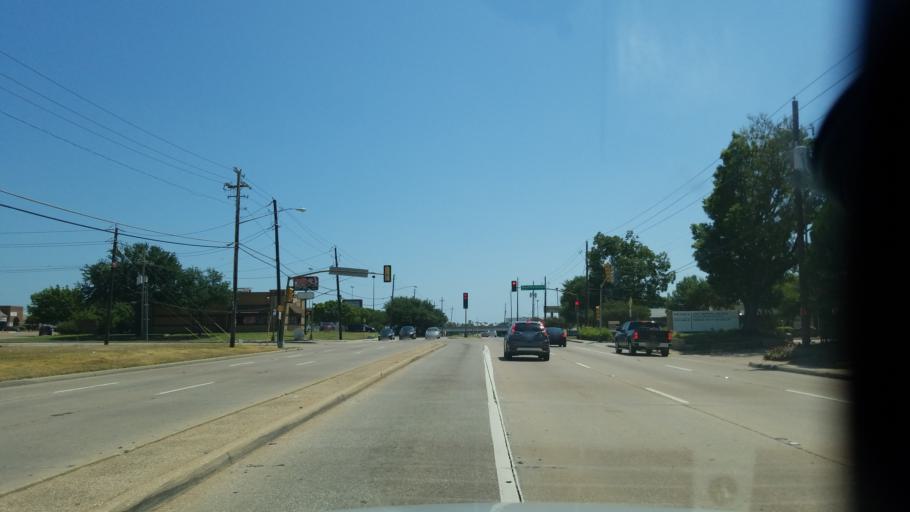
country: US
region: Texas
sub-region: Dallas County
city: Duncanville
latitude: 32.6475
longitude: -96.8883
